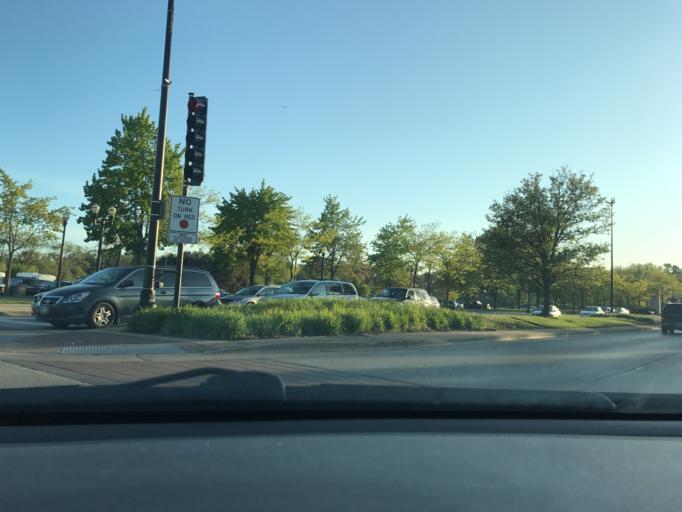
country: US
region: Illinois
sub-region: Kane County
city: Elgin
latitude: 42.0419
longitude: -88.2869
